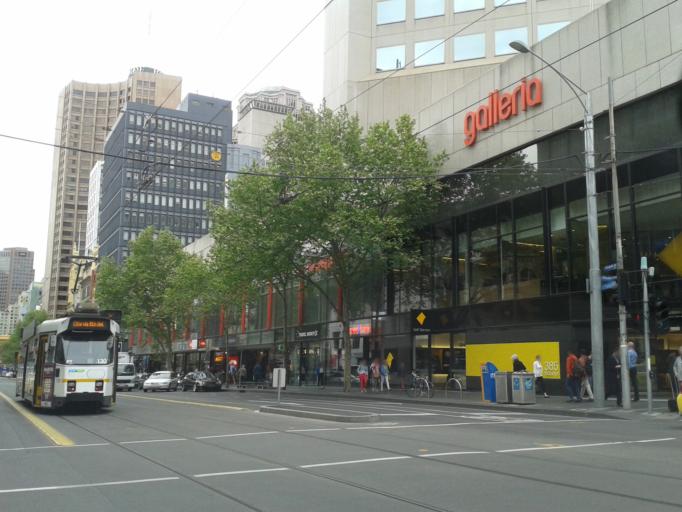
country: AU
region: Victoria
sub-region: Melbourne
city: Melbourne
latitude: -37.8142
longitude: 144.9630
